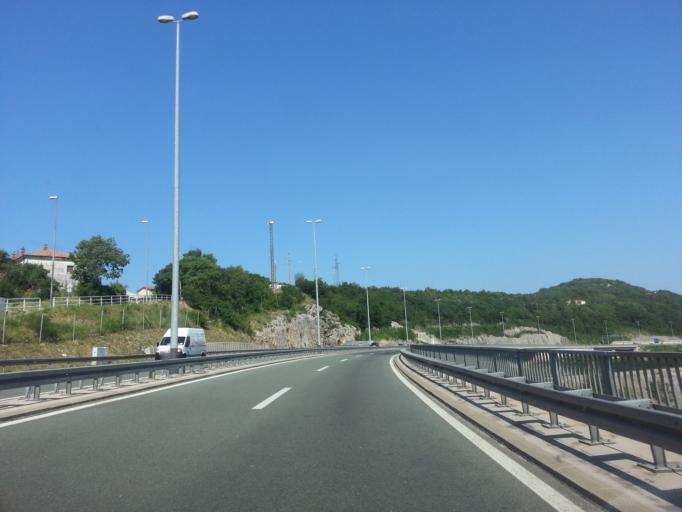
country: HR
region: Primorsko-Goranska
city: Cavle
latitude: 45.3273
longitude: 14.4787
